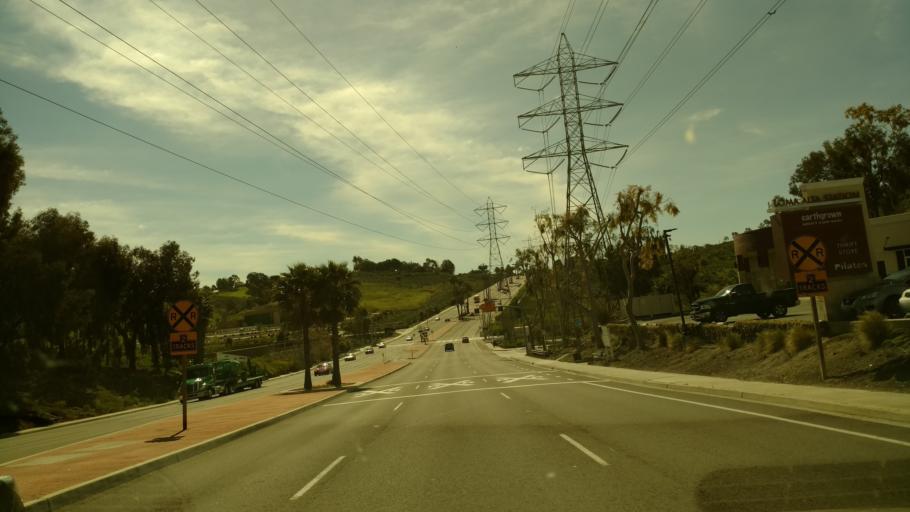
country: US
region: California
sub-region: San Diego County
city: Carlsbad
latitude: 33.2013
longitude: -117.3321
